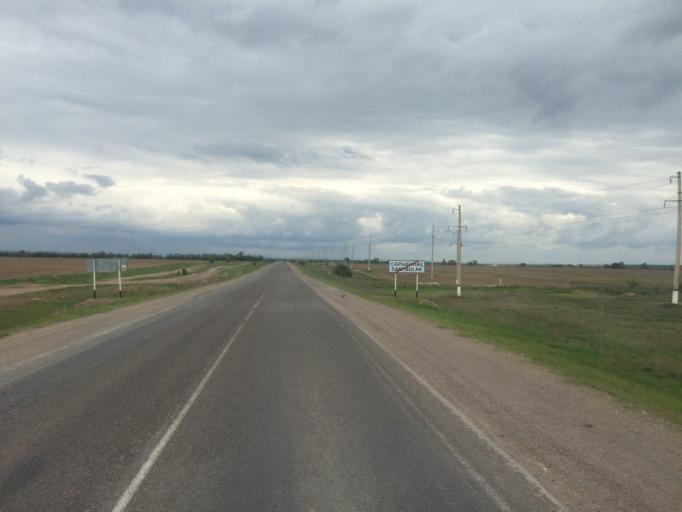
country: KG
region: Chuy
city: Sokuluk
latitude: 43.2459
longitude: 74.3034
